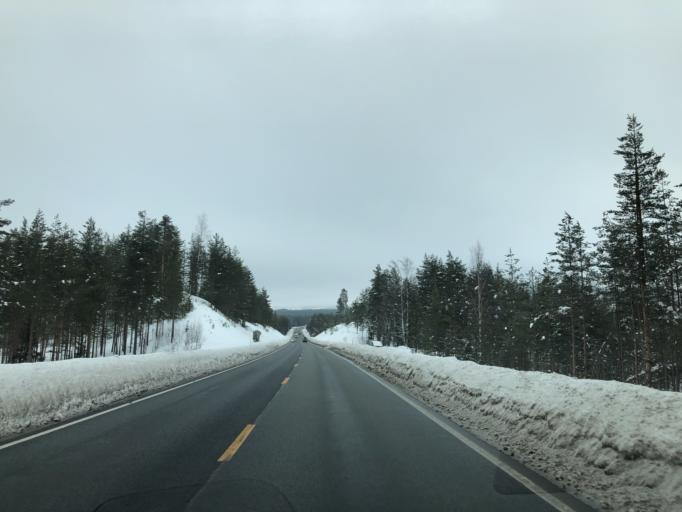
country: NO
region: Hedmark
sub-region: Elverum
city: Elverum
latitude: 60.9912
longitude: 11.7658
